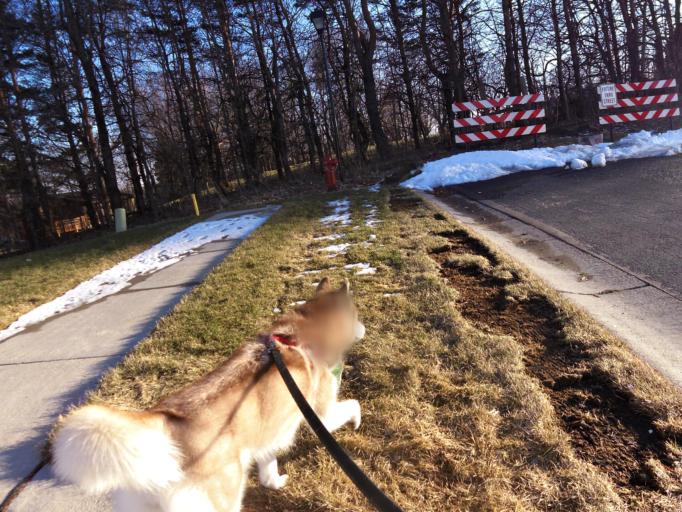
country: US
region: Minnesota
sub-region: Scott County
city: Prior Lake
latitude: 44.6920
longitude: -93.4476
